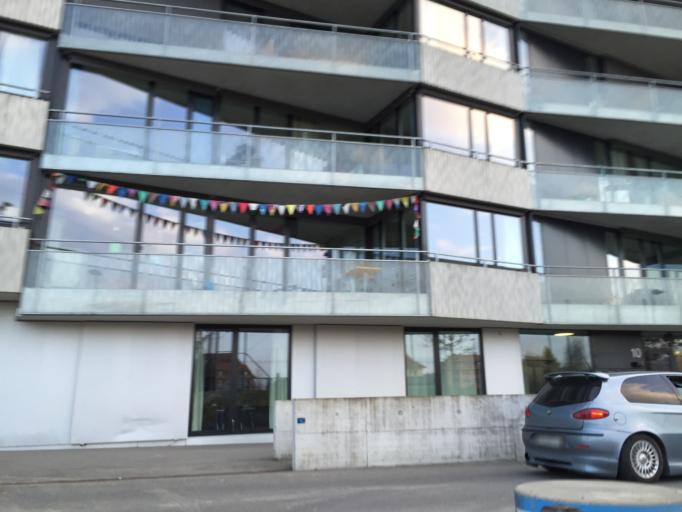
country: CH
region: Bern
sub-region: Bern-Mittelland District
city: Koniz
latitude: 46.9366
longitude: 7.4191
